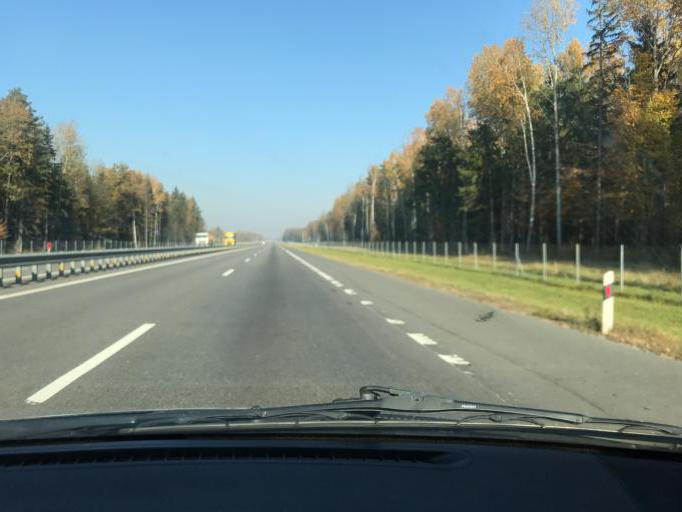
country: BY
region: Minsk
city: Slutsk
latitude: 53.2421
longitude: 27.5504
